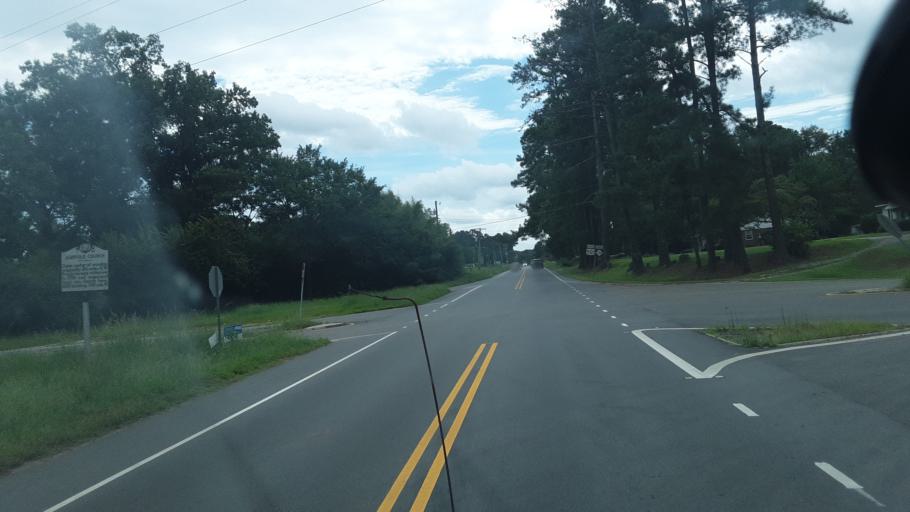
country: US
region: North Carolina
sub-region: Robeson County
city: Rowland
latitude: 34.5496
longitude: -79.3069
